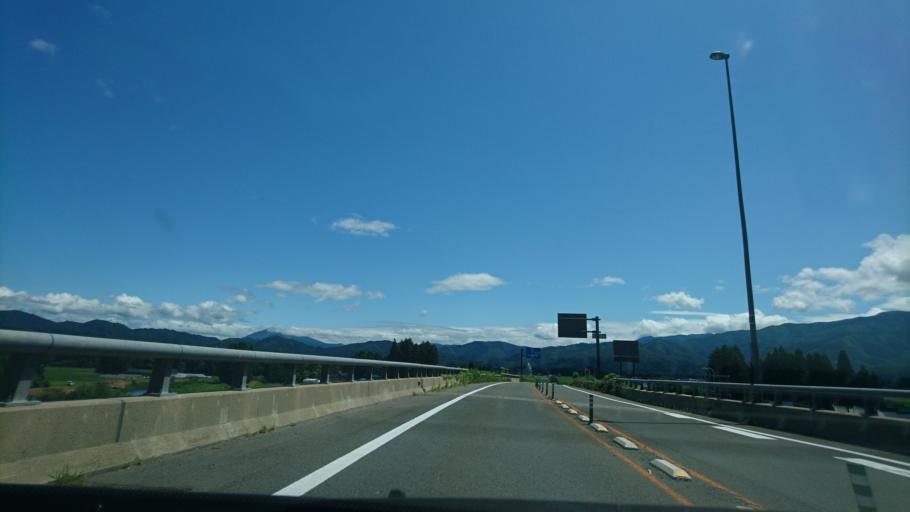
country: JP
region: Akita
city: Kakunodatemachi
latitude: 39.6134
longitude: 140.5753
